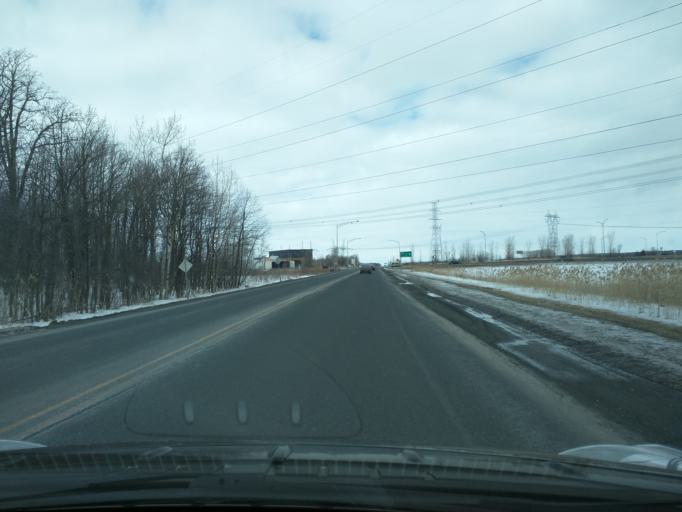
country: CA
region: Quebec
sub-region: Monteregie
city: Sainte-Julie
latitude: 45.6029
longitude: -73.3777
